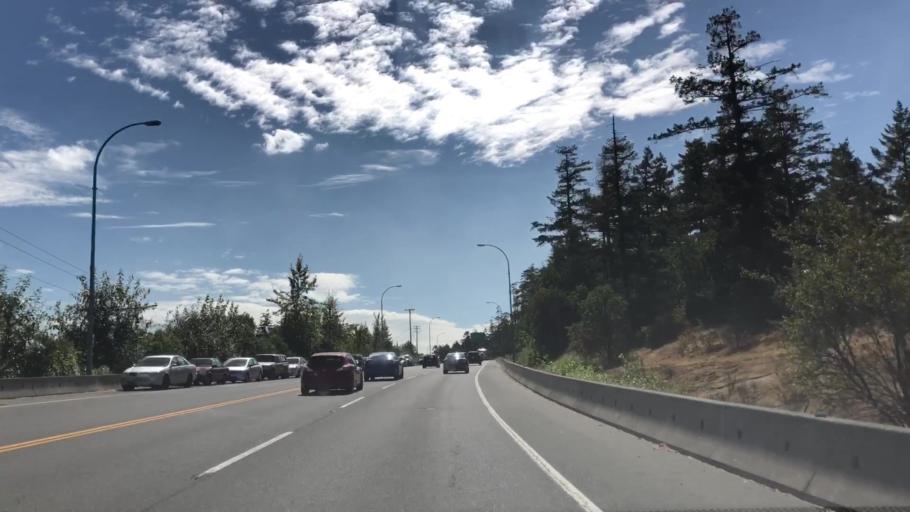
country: CA
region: British Columbia
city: Nanaimo
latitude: 49.1487
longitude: -123.8873
